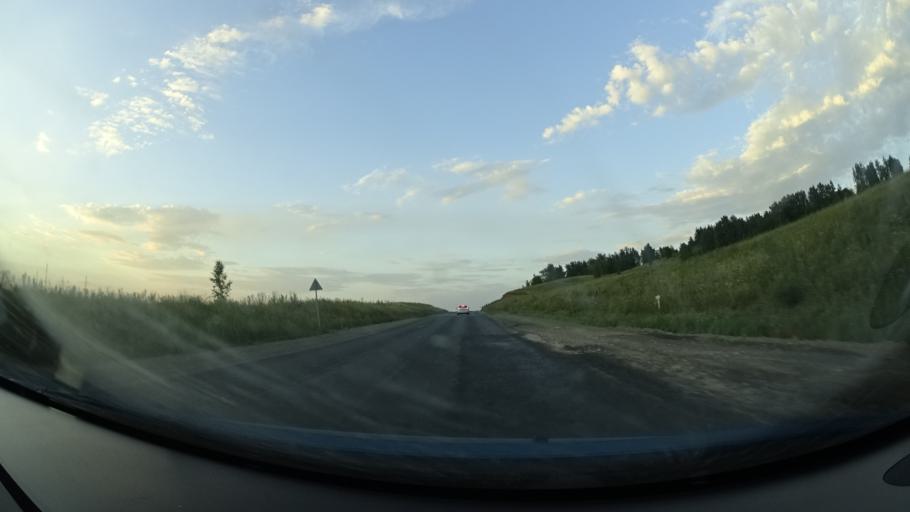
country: RU
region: Orenburg
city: Severnoye
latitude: 54.1702
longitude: 52.6442
